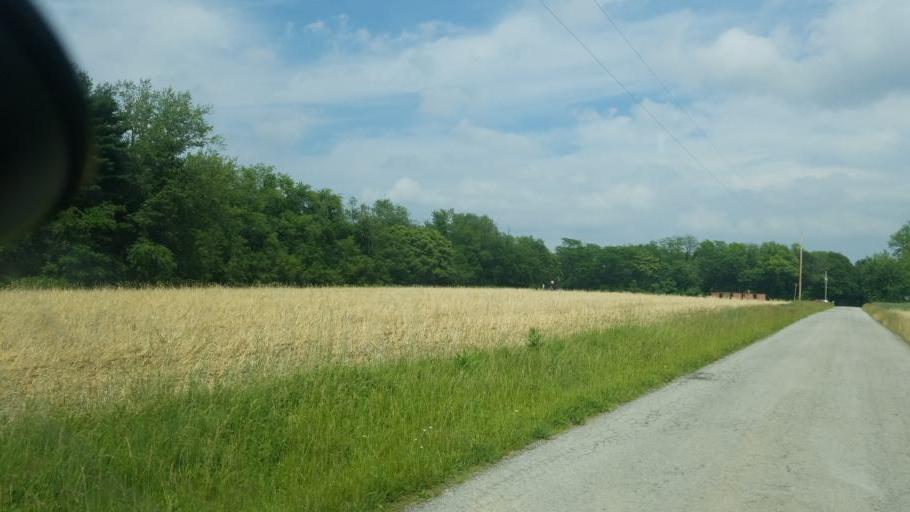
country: US
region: Ohio
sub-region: Knox County
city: Oak Hill
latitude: 40.3119
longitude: -82.1891
